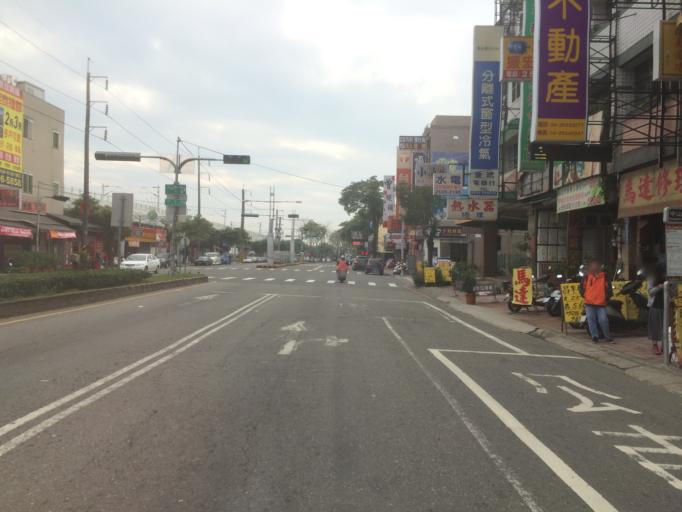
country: TW
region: Taiwan
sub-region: Taichung City
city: Taichung
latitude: 24.1875
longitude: 120.7024
